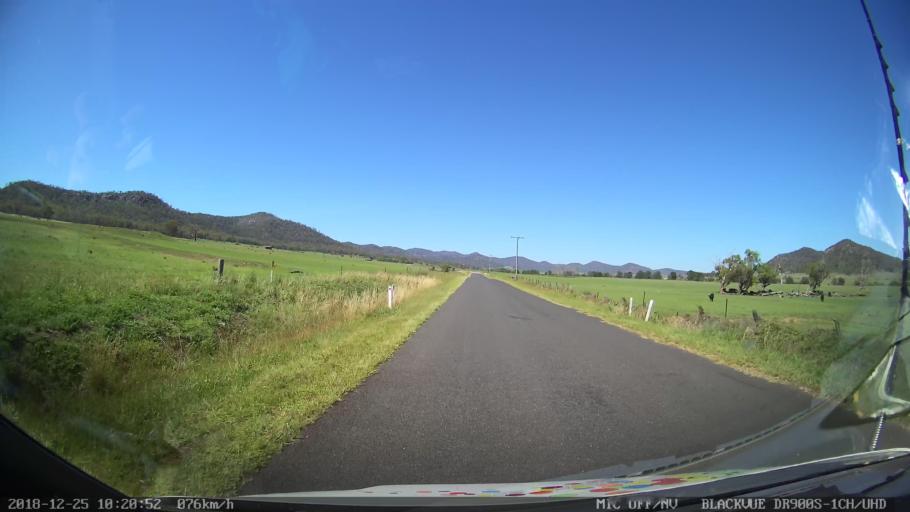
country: AU
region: New South Wales
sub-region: Muswellbrook
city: Denman
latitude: -32.3616
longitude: 150.5451
